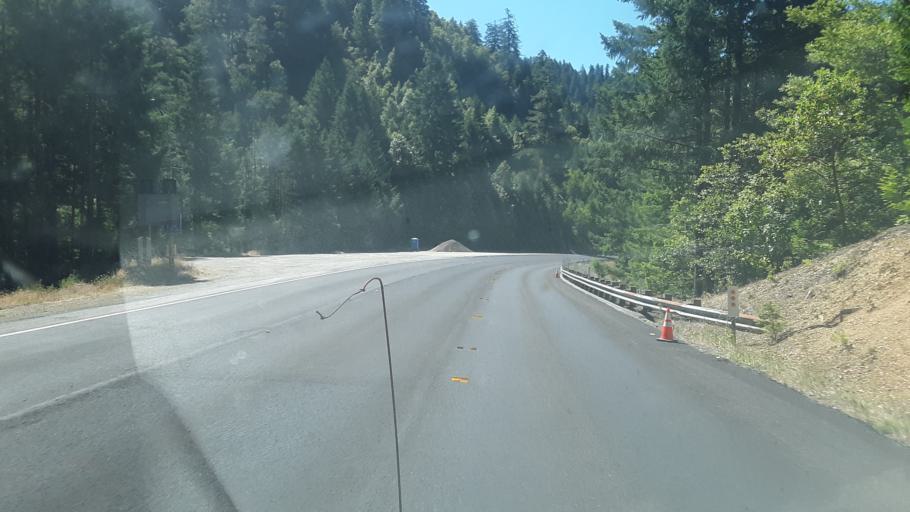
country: US
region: Oregon
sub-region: Josephine County
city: Cave Junction
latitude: 41.9560
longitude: -123.7437
